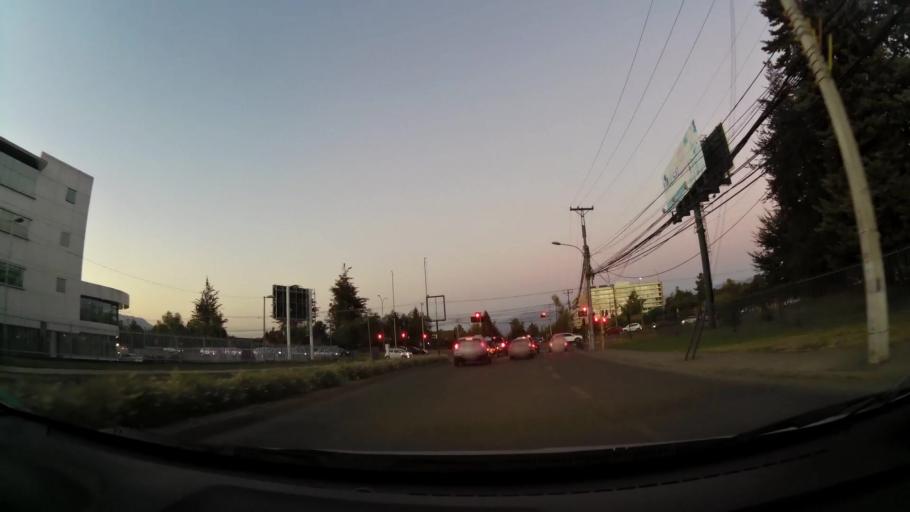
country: CL
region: O'Higgins
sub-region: Provincia de Cachapoal
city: Rancagua
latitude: -34.1860
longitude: -70.7220
